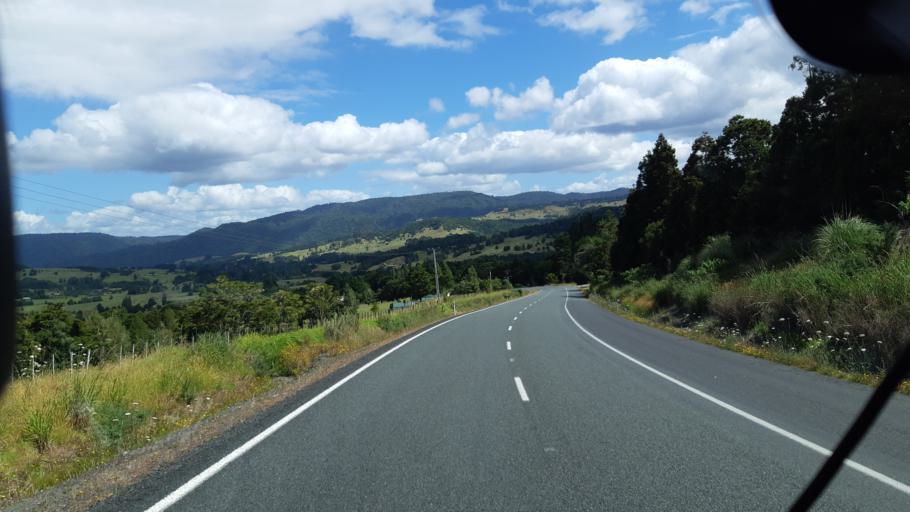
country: NZ
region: Northland
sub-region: Far North District
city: Waimate North
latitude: -35.3181
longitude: 173.7594
